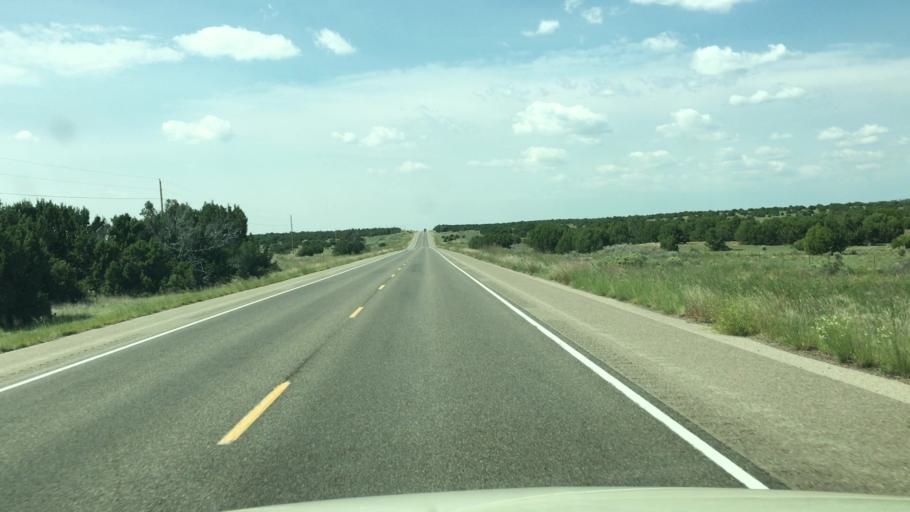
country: US
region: New Mexico
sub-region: Torrance County
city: Moriarty
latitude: 35.0498
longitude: -105.6874
